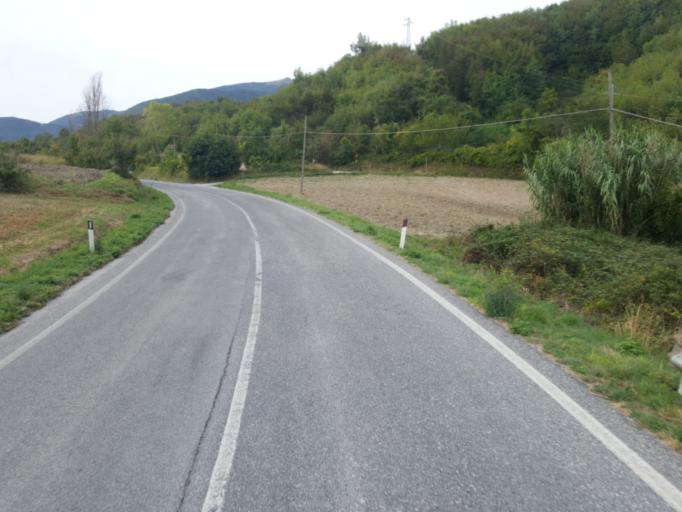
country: IT
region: Umbria
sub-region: Provincia di Perugia
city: Fossato di Vico
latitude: 43.3085
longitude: 12.8242
